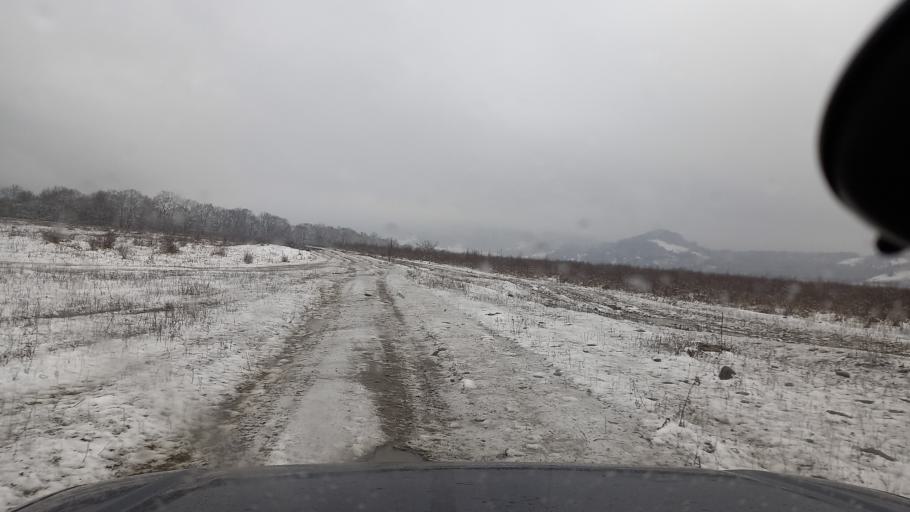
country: RU
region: Adygeya
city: Kamennomostskiy
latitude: 44.2209
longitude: 40.1800
